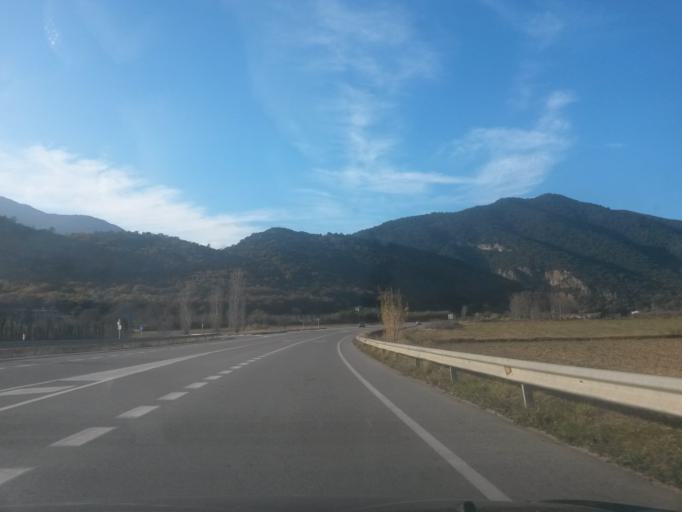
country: ES
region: Catalonia
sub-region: Provincia de Girona
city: la Cellera de Ter
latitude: 41.9790
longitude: 2.6144
